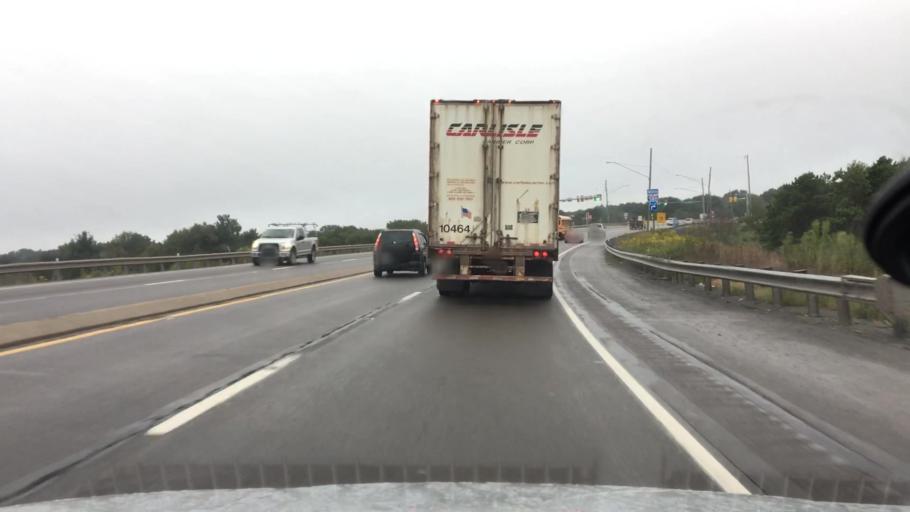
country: US
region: Pennsylvania
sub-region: Monroe County
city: Emerald Lakes
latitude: 41.1064
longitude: -75.3946
